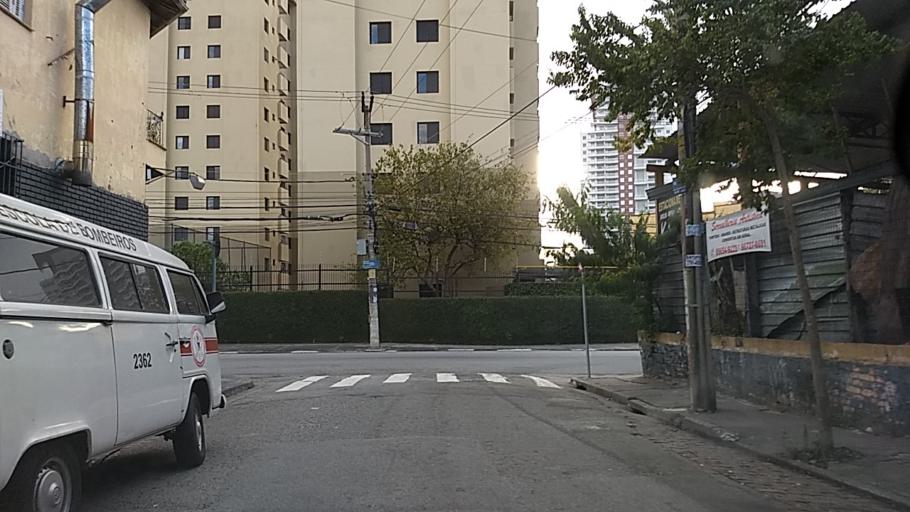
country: BR
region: Sao Paulo
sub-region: Sao Paulo
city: Sao Paulo
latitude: -23.4965
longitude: -46.6103
